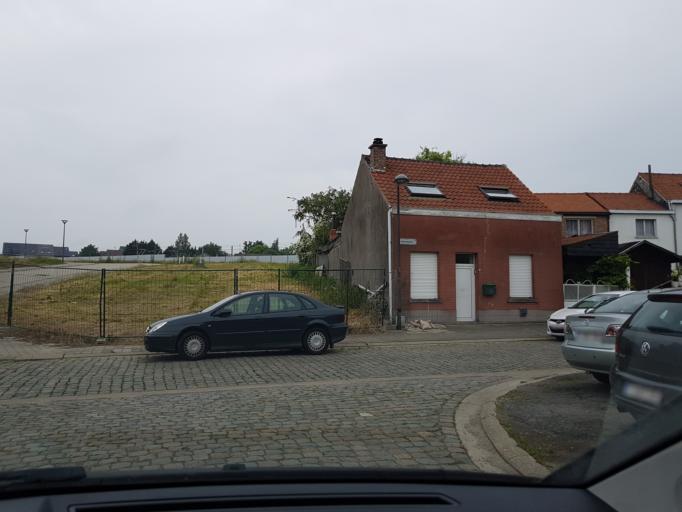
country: BE
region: Flanders
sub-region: Provincie Vlaams-Brabant
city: Zaventem
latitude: 50.8820
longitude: 4.4831
